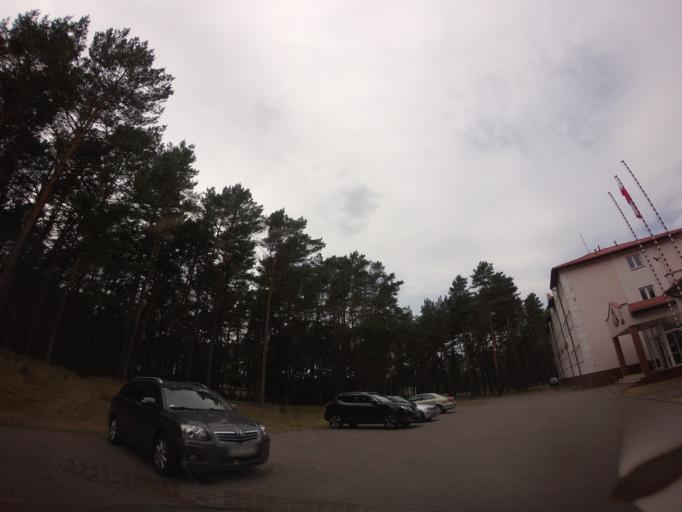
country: PL
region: West Pomeranian Voivodeship
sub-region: Powiat szczecinecki
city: Borne Sulinowo
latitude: 53.5841
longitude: 16.5159
